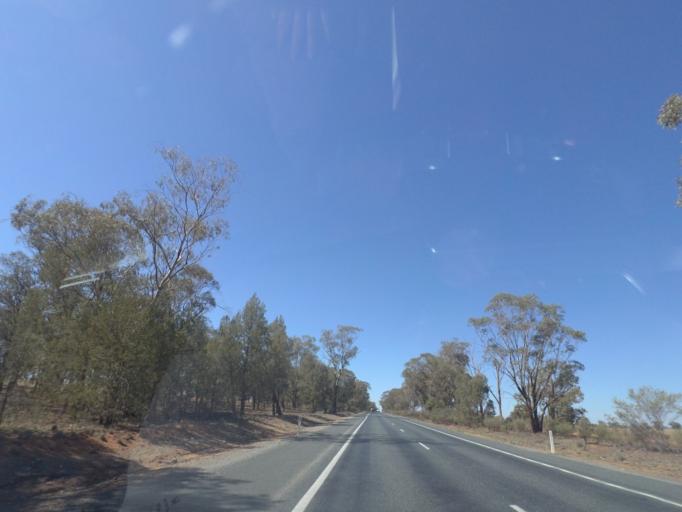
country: AU
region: New South Wales
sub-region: Bland
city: West Wyalong
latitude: -34.2080
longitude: 147.1092
